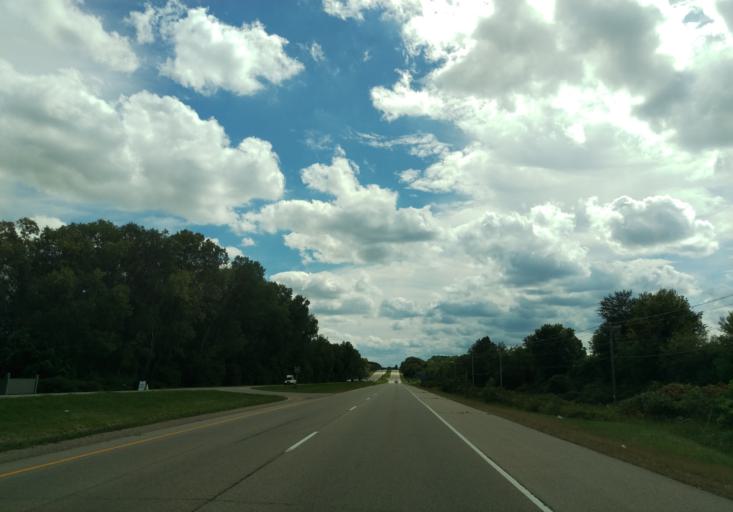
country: US
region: Wisconsin
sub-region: Dane County
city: Maple Bluff
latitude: 43.1492
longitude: -89.4003
